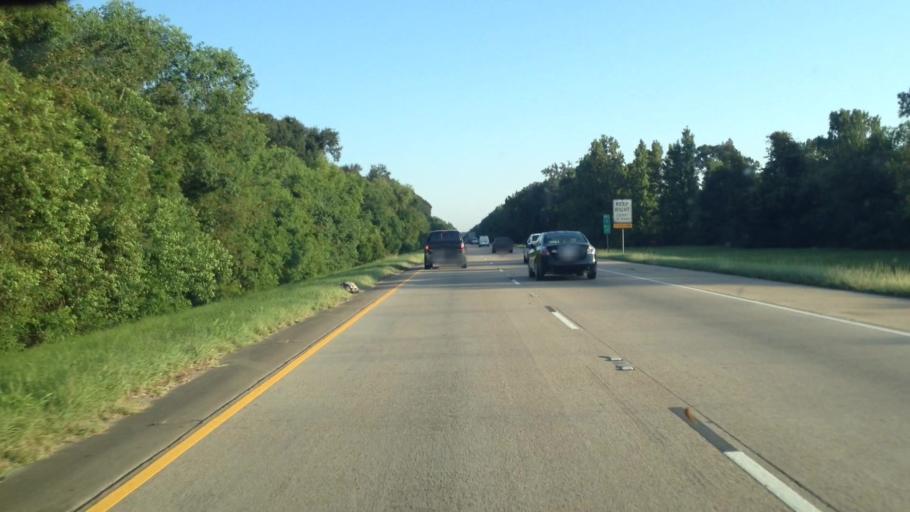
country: US
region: Louisiana
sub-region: Ascension Parish
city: Prairieville
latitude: 30.2844
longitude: -90.9893
